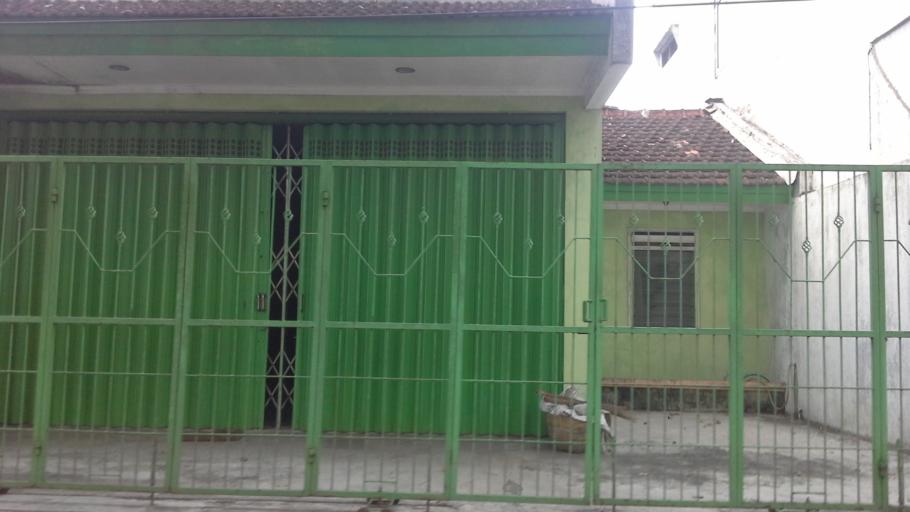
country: ID
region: East Java
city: Bondowoso
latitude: -7.9306
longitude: 113.8192
